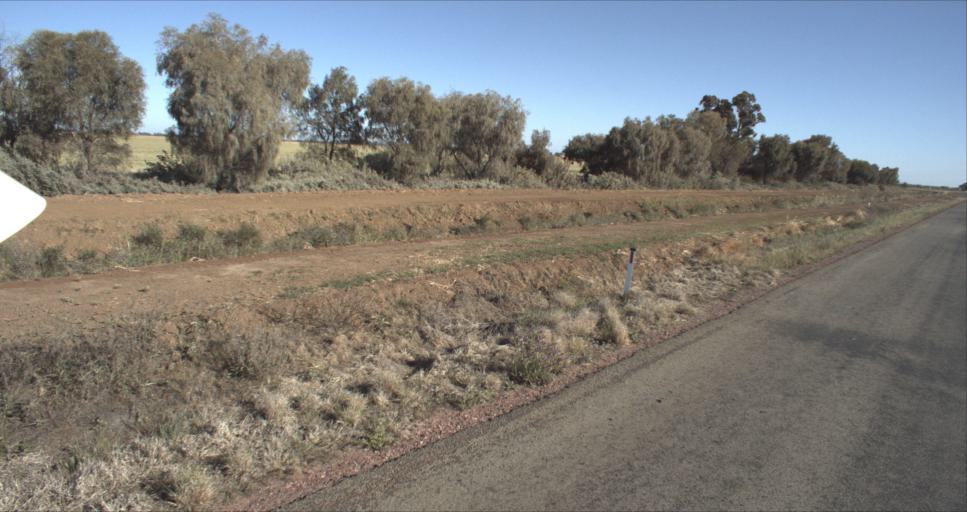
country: AU
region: New South Wales
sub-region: Leeton
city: Leeton
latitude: -34.5535
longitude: 146.2669
